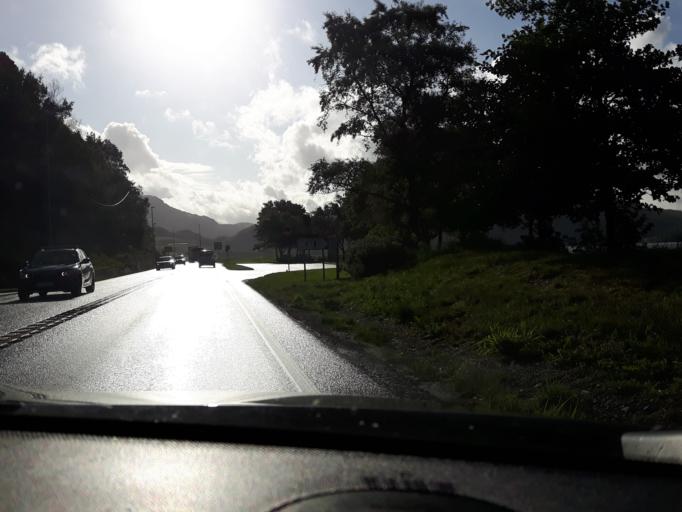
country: NO
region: Rogaland
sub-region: Gjesdal
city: Algard
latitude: 58.7663
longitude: 5.8711
